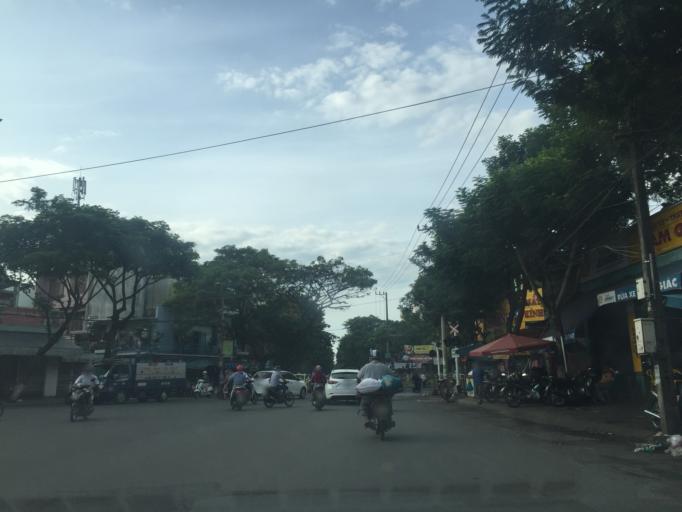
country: VN
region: Da Nang
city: Da Nang
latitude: 16.0727
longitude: 108.2130
